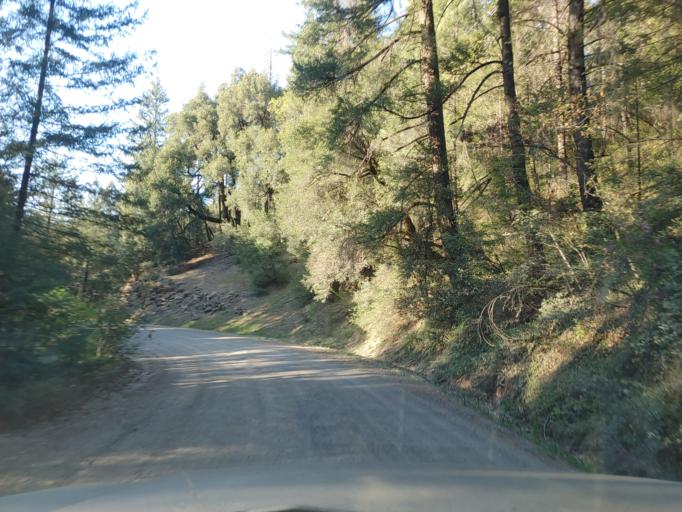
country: US
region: California
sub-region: Shasta County
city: Bella Vista
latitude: 40.8142
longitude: -122.0059
